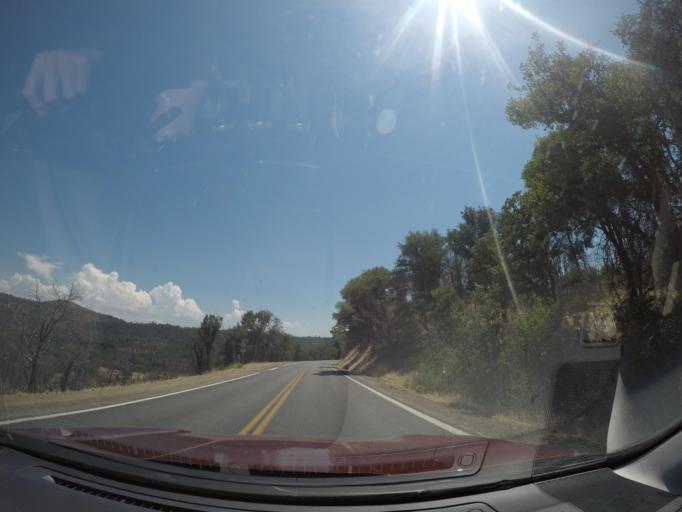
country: US
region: California
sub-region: Shasta County
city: Burney
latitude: 40.9955
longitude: -121.5116
